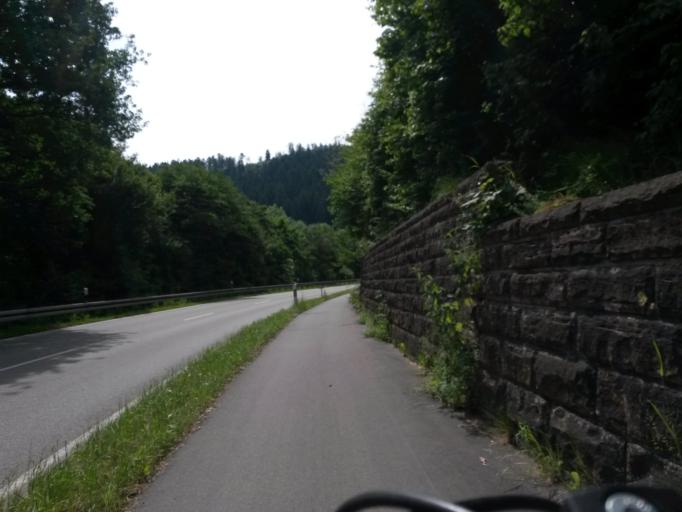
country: DE
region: Baden-Wuerttemberg
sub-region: Karlsruhe Region
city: Calw
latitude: 48.6907
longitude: 8.7310
